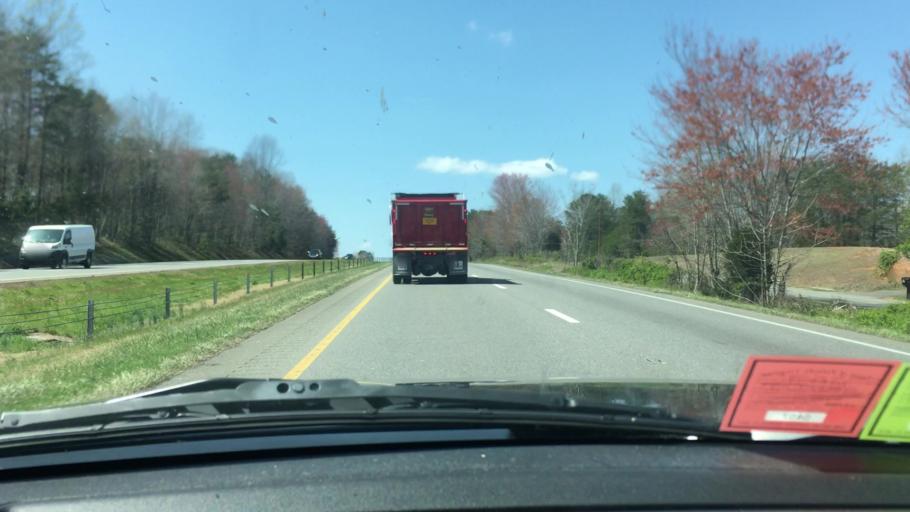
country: US
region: North Carolina
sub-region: Surry County
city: Pilot Mountain
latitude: 36.4266
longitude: -80.5212
